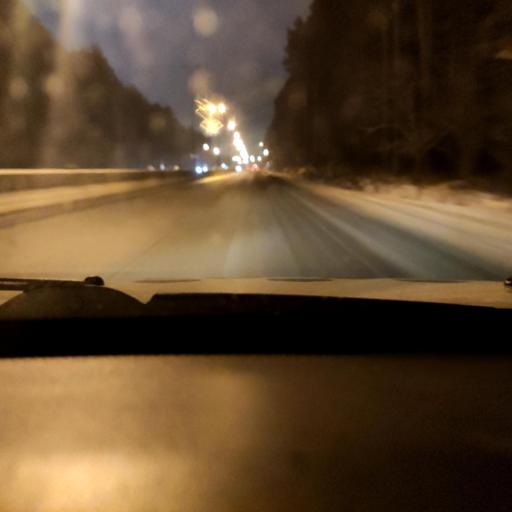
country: RU
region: Perm
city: Perm
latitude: 58.0464
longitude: 56.1844
